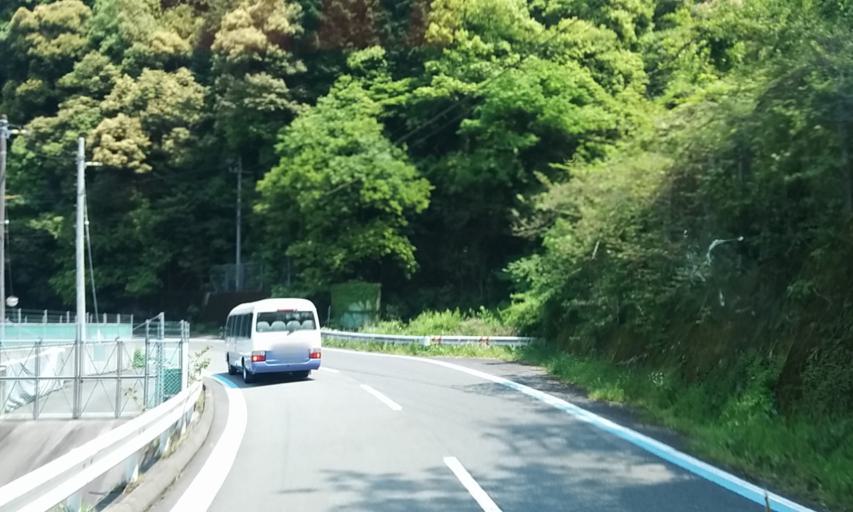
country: JP
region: Ehime
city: Niihama
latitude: 33.8994
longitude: 133.3104
